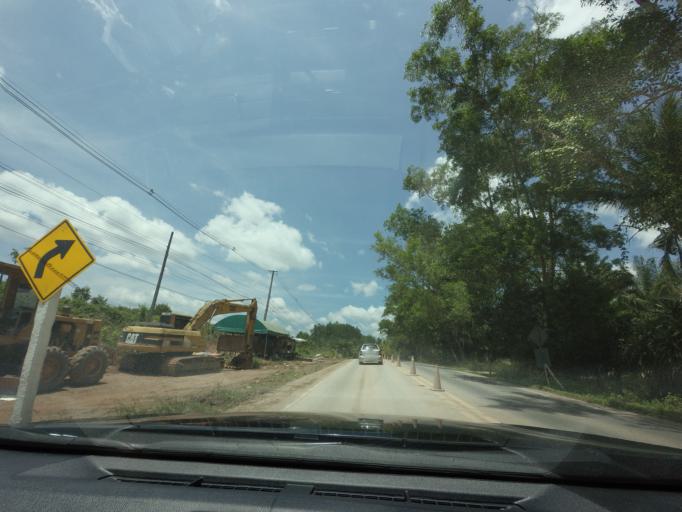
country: TH
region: Chumphon
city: Ban Nam Yuen
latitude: 9.9013
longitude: 98.8942
